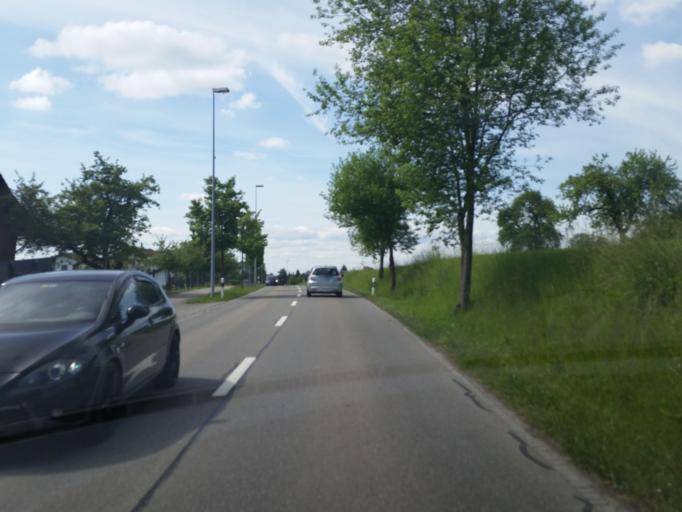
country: CH
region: Aargau
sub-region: Bezirk Bremgarten
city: Unterlunkhofen
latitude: 47.3372
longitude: 8.3857
